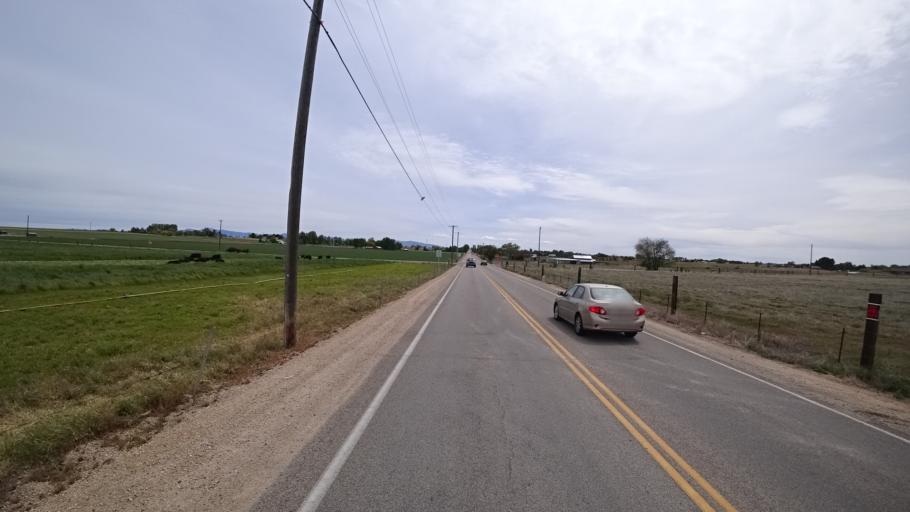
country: US
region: Idaho
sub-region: Ada County
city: Kuna
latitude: 43.5612
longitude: -116.4549
